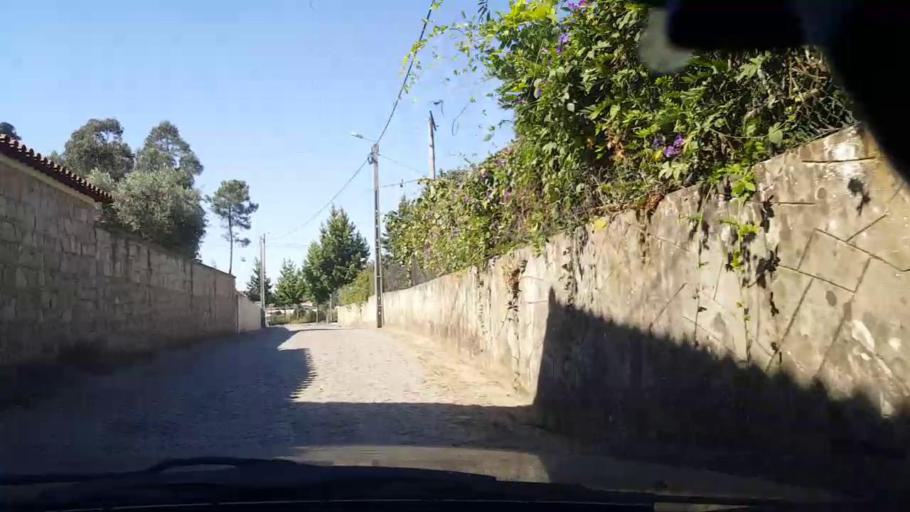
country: PT
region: Braga
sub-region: Vila Nova de Famalicao
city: Ribeirao
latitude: 41.3557
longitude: -8.6320
